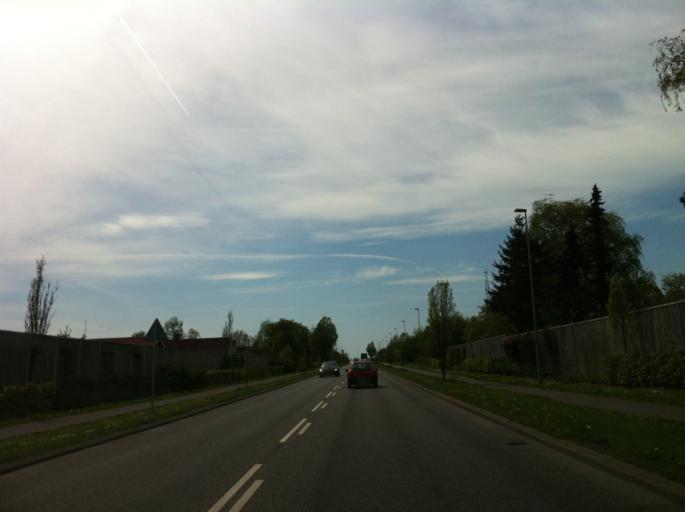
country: DK
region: Zealand
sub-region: Naestved Kommune
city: Naestved
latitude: 55.2158
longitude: 11.7669
